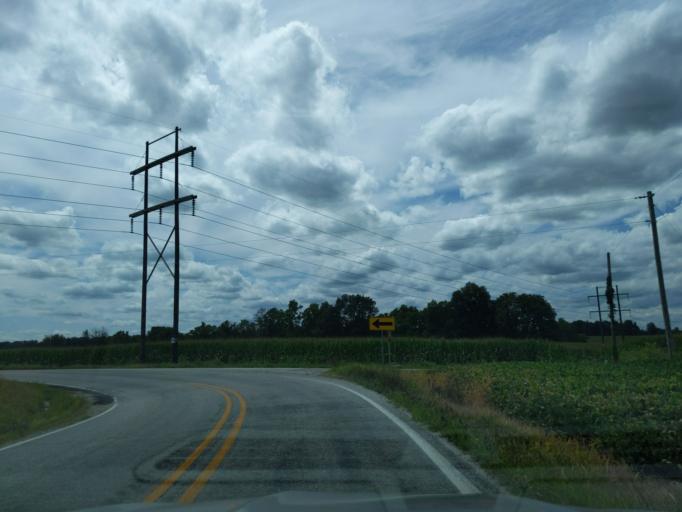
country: US
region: Indiana
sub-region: Ripley County
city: Osgood
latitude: 39.2152
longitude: -85.2754
